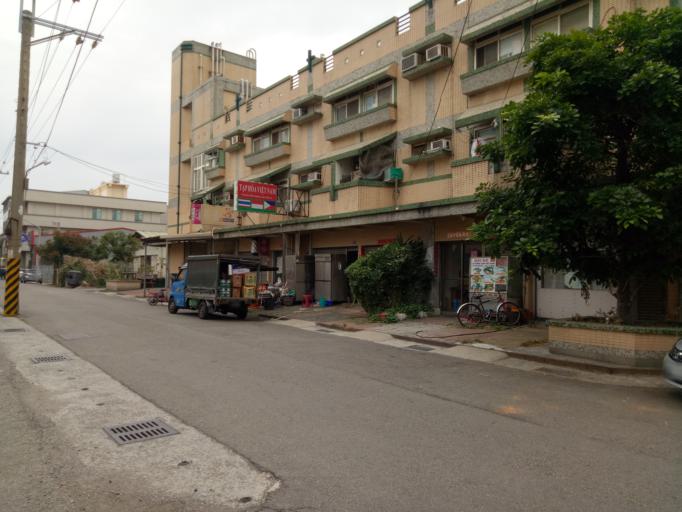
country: TW
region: Taiwan
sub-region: Changhua
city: Chang-hua
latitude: 24.2415
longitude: 120.5301
